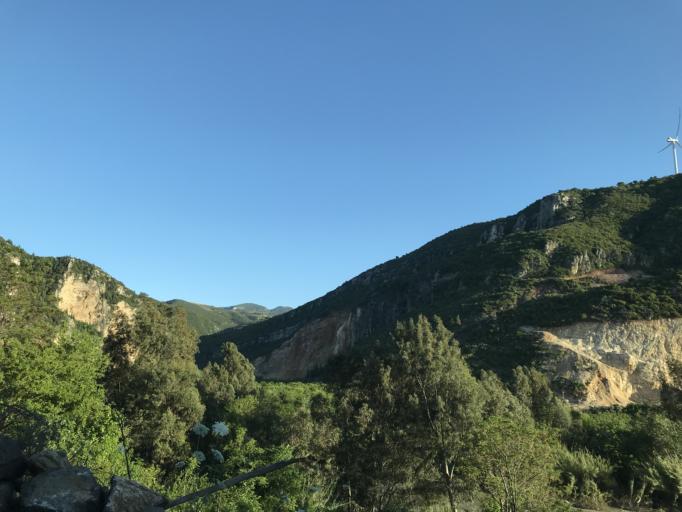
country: TR
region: Hatay
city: Samandag
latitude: 36.0767
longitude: 36.0263
